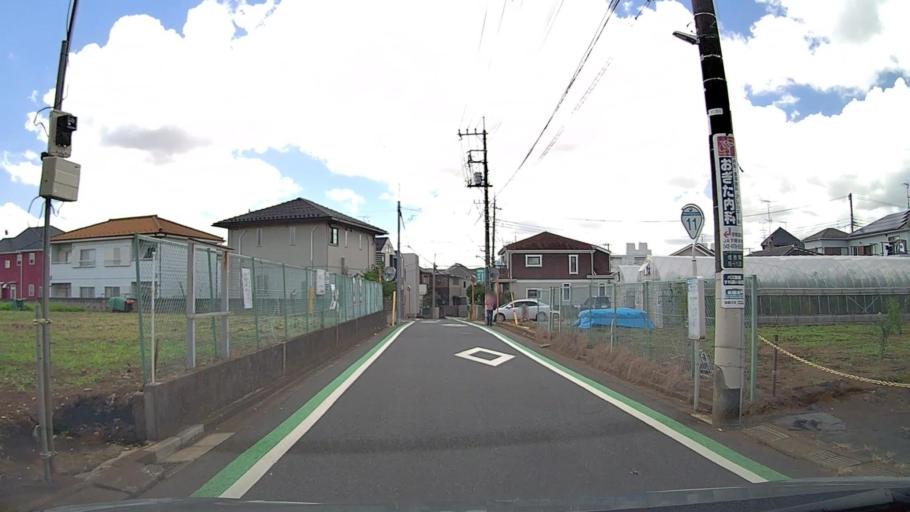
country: JP
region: Tokyo
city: Nishi-Tokyo-shi
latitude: 35.7469
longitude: 139.5583
